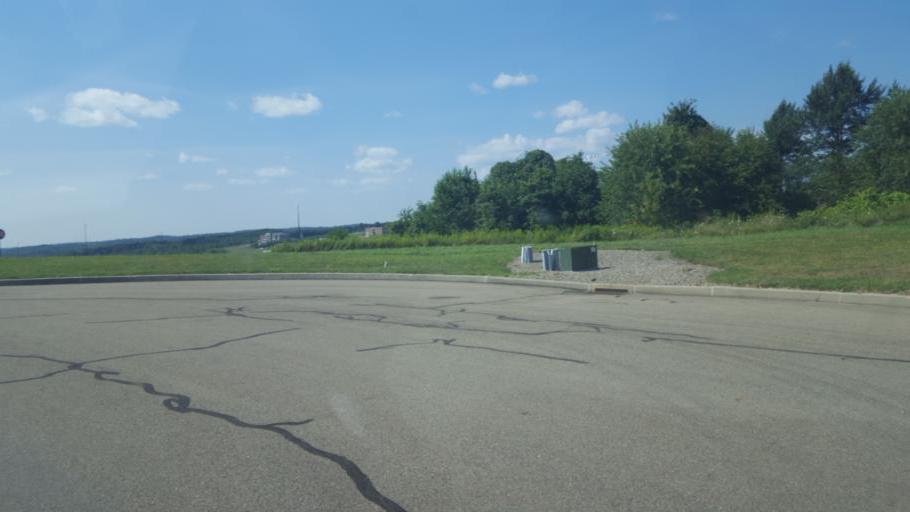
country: US
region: Pennsylvania
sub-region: Clarion County
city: Clarion
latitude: 41.1836
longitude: -79.3886
